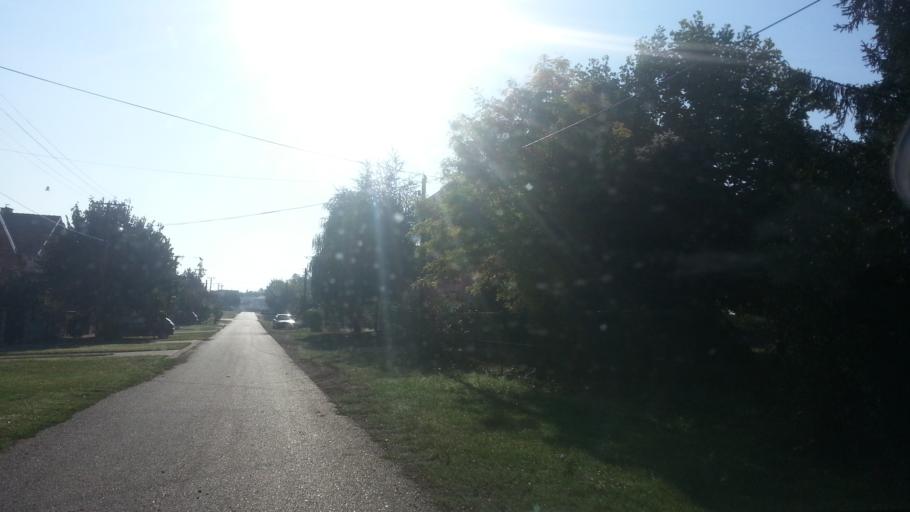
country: RS
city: Stari Banovci
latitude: 44.9834
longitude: 20.2666
